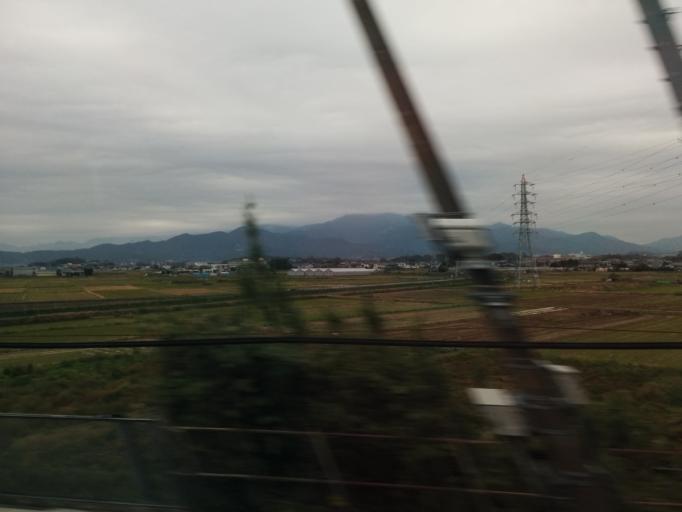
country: JP
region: Kanagawa
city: Isehara
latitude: 35.3663
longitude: 139.3351
